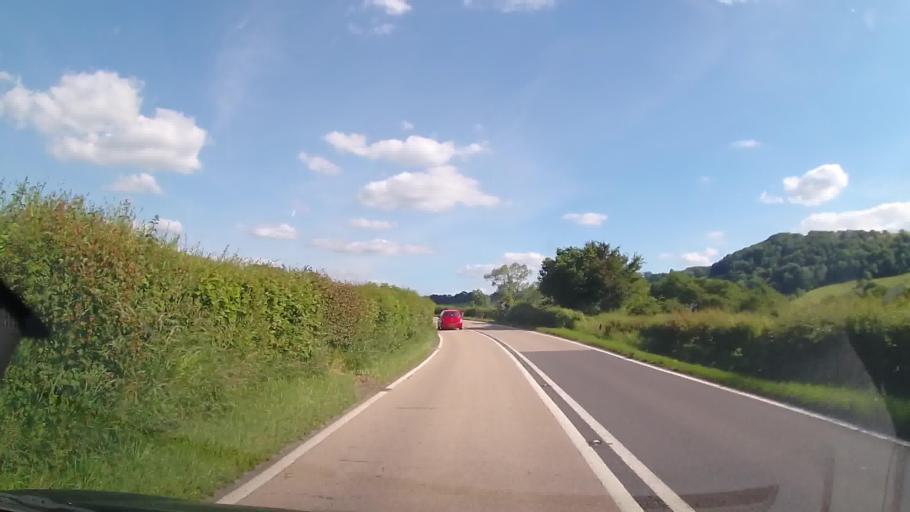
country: GB
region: Wales
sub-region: Sir Powys
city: Welshpool
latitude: 52.6515
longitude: -3.2511
